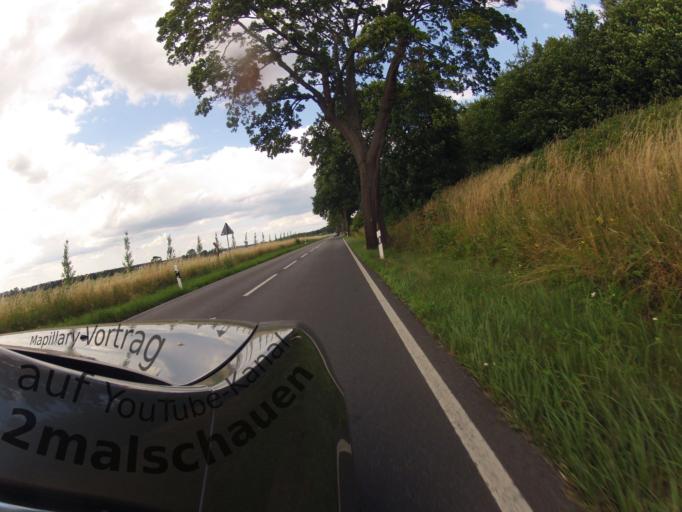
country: DE
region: Mecklenburg-Vorpommern
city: Seebad Heringsdorf
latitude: 53.9018
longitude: 14.1476
